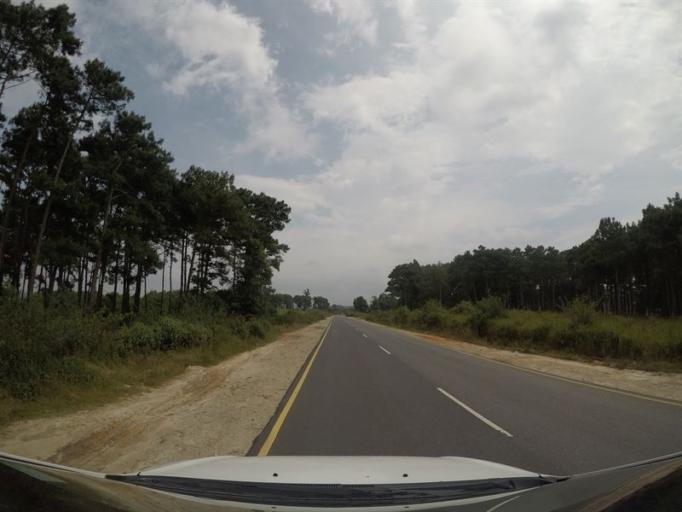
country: IN
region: Meghalaya
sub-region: East Khasi Hills
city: Shillong
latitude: 25.4896
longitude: 92.1899
